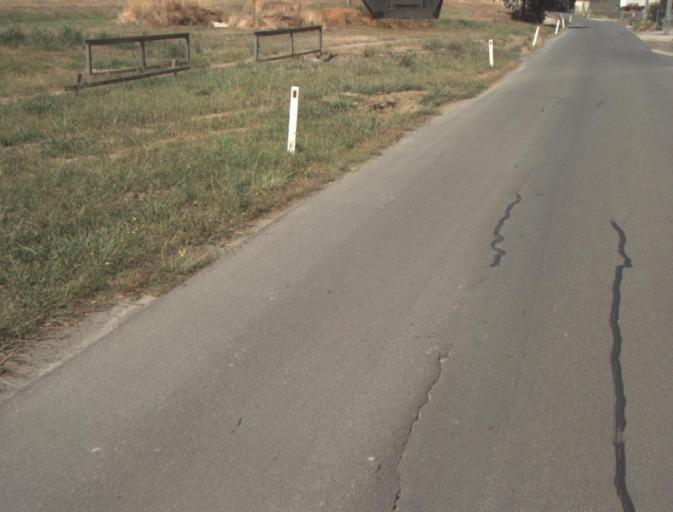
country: AU
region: Tasmania
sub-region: Launceston
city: East Launceston
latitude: -41.4189
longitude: 147.1430
